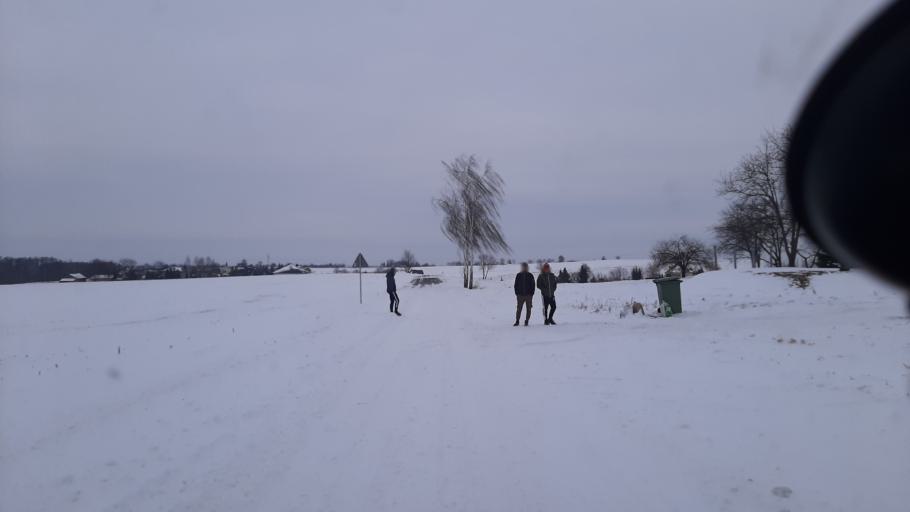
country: PL
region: Lublin Voivodeship
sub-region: Powiat lubelski
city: Garbow
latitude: 51.3349
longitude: 22.2923
